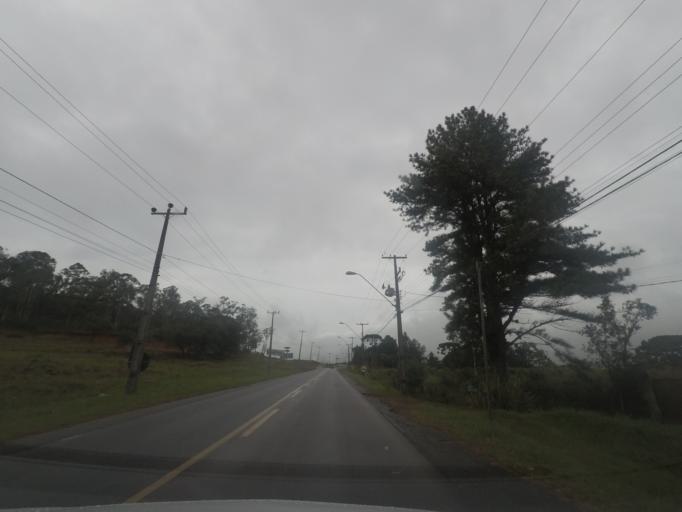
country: BR
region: Parana
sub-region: Campina Grande Do Sul
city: Campina Grande do Sul
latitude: -25.3258
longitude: -49.0784
